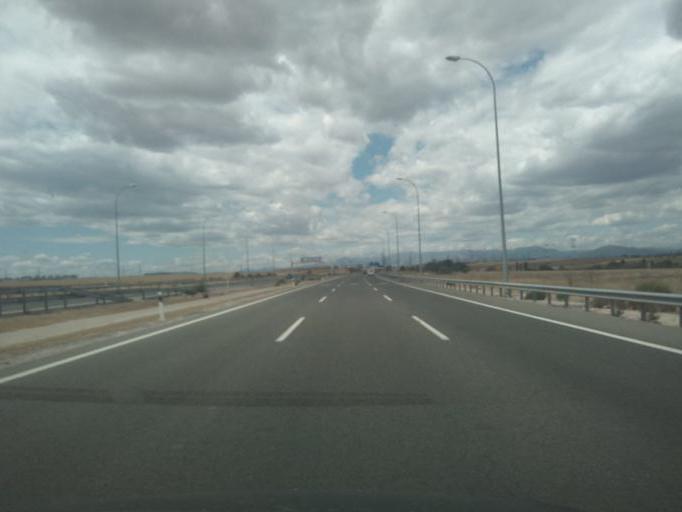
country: ES
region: Madrid
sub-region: Provincia de Madrid
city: San Sebastian de los Reyes
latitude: 40.5495
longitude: -3.5776
